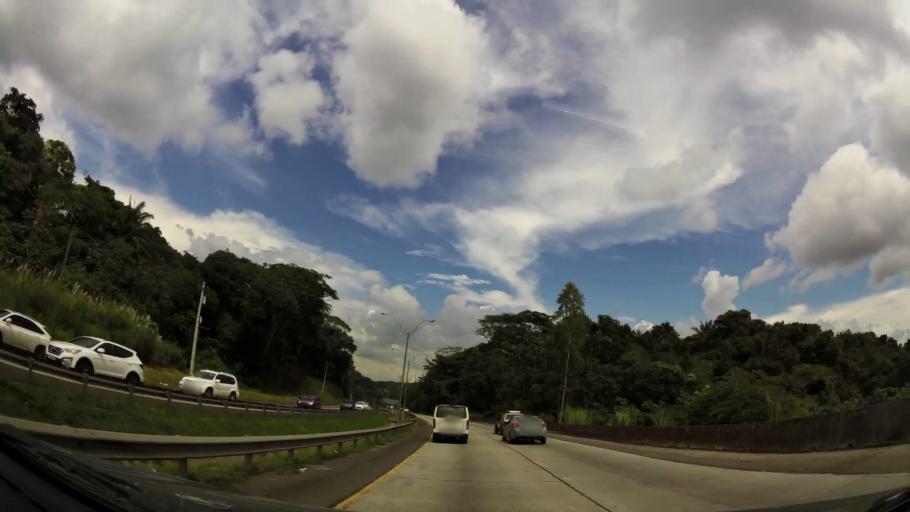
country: PA
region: Panama
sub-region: Distrito de Panama
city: Paraiso
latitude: 9.0113
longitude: -79.6456
